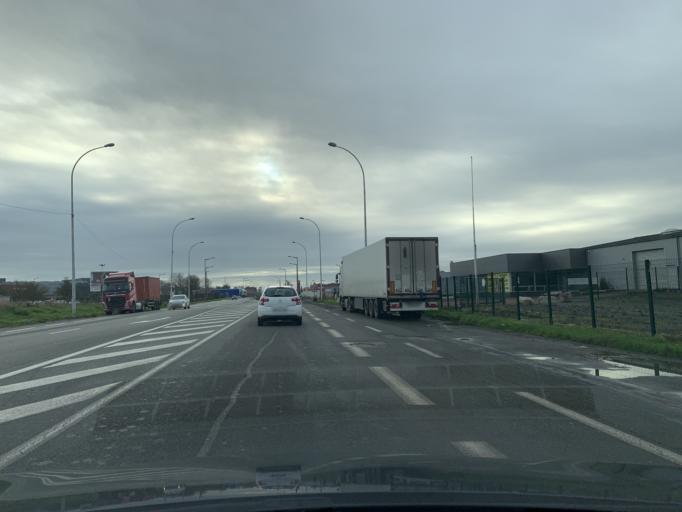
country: FR
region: Nord-Pas-de-Calais
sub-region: Departement du Nord
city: Dechy
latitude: 50.3418
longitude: 3.0952
